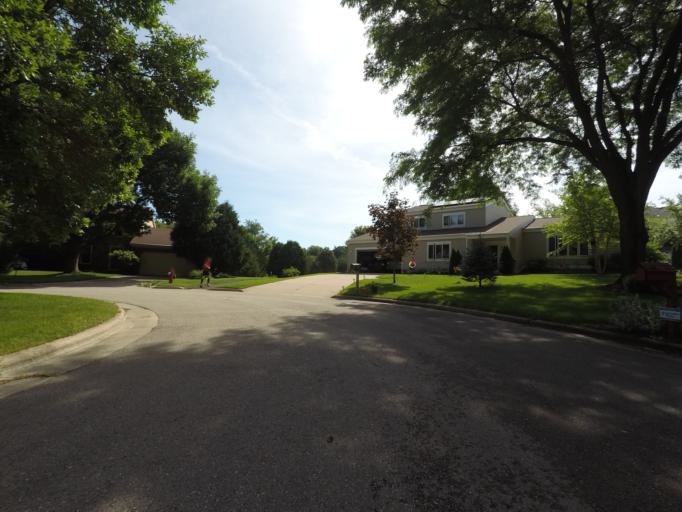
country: US
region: Wisconsin
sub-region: Dane County
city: Middleton
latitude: 43.0767
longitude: -89.5052
